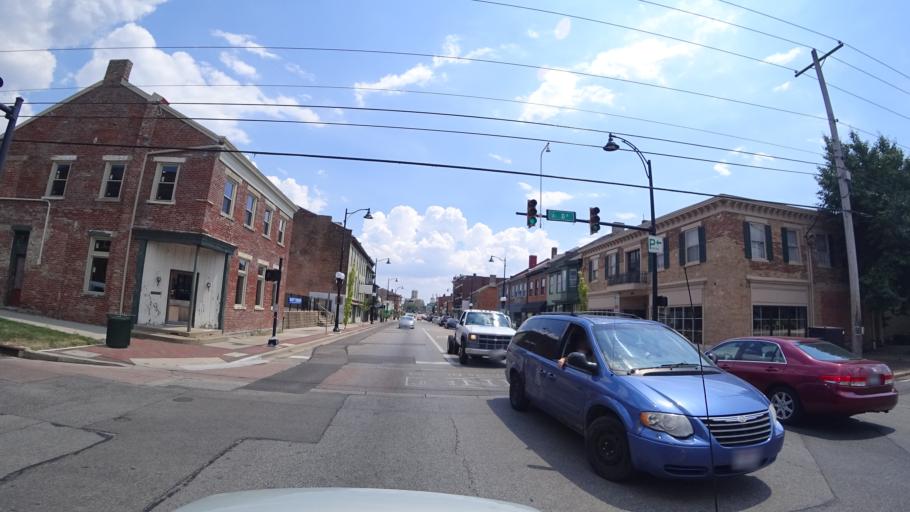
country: US
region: Ohio
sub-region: Butler County
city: Hamilton
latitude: 39.4039
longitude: -84.5691
